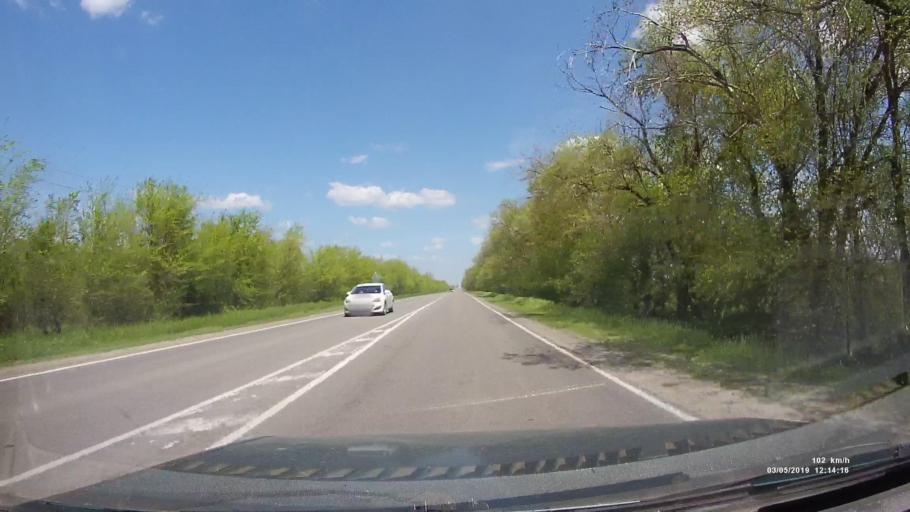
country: RU
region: Rostov
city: Melikhovskaya
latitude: 47.3416
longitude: 40.5616
